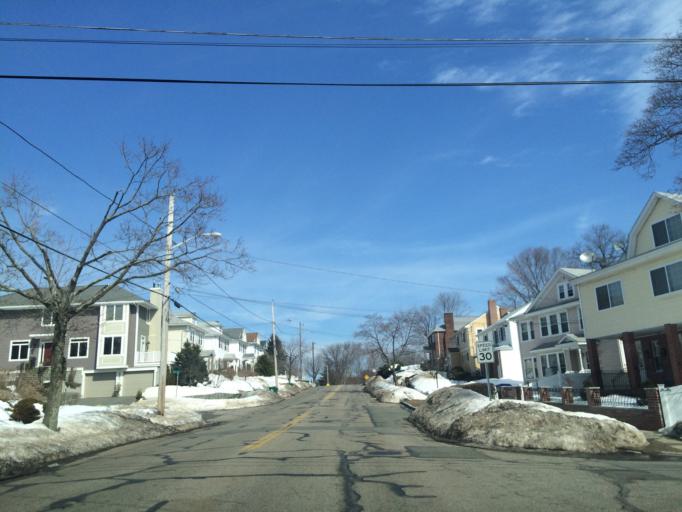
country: US
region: Massachusetts
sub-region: Middlesex County
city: Medford
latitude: 42.4268
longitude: -71.1051
